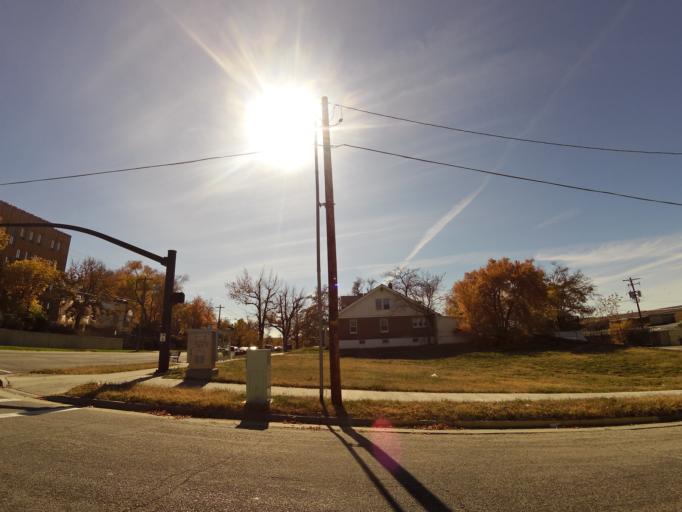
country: US
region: Utah
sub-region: Weber County
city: Ogden
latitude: 41.2206
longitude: -111.9680
